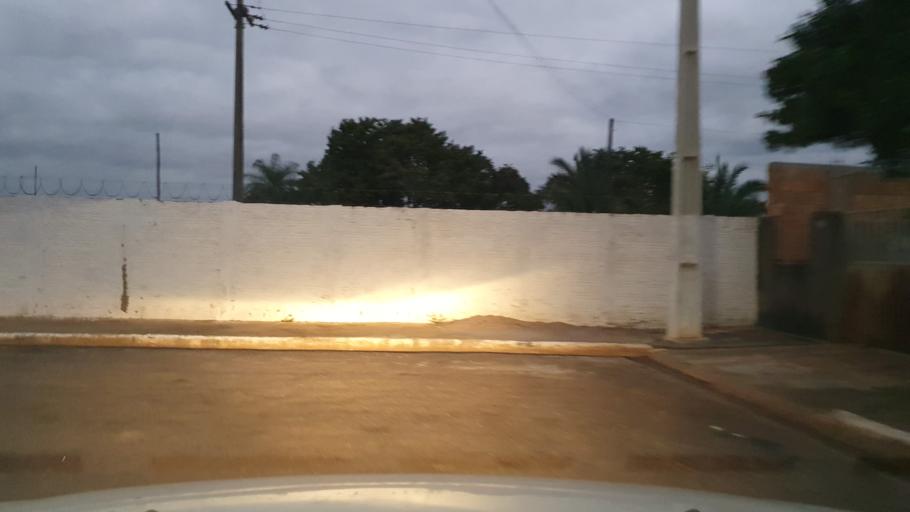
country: BR
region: Mato Grosso
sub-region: Pontes E Lacerda
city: Pontes e Lacerda
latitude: -15.2353
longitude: -59.3143
